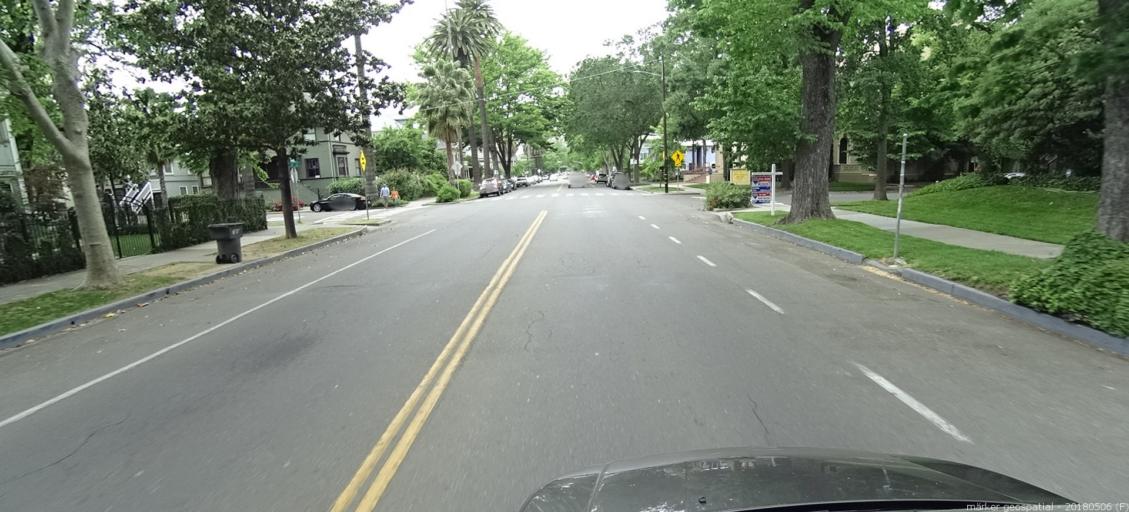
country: US
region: California
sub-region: Sacramento County
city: Sacramento
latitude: 38.5722
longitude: -121.4769
